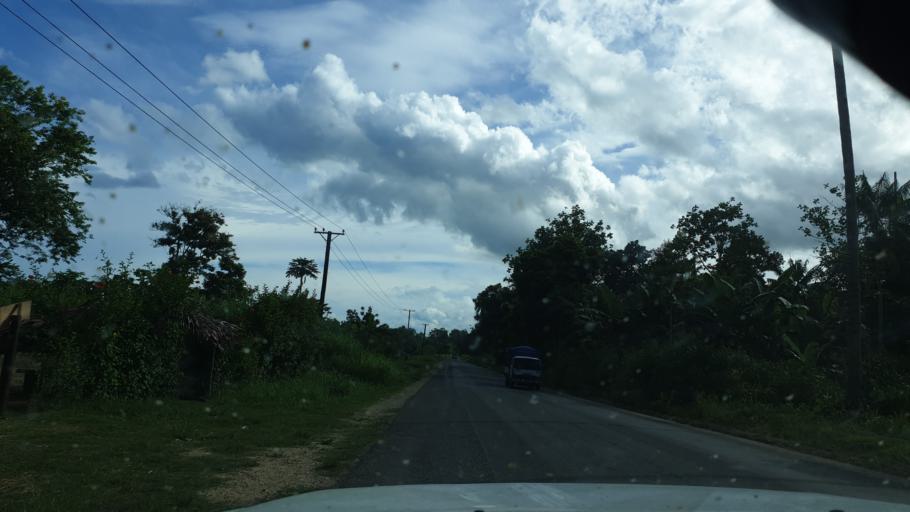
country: PG
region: Madang
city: Madang
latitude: -5.1029
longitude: 145.7933
